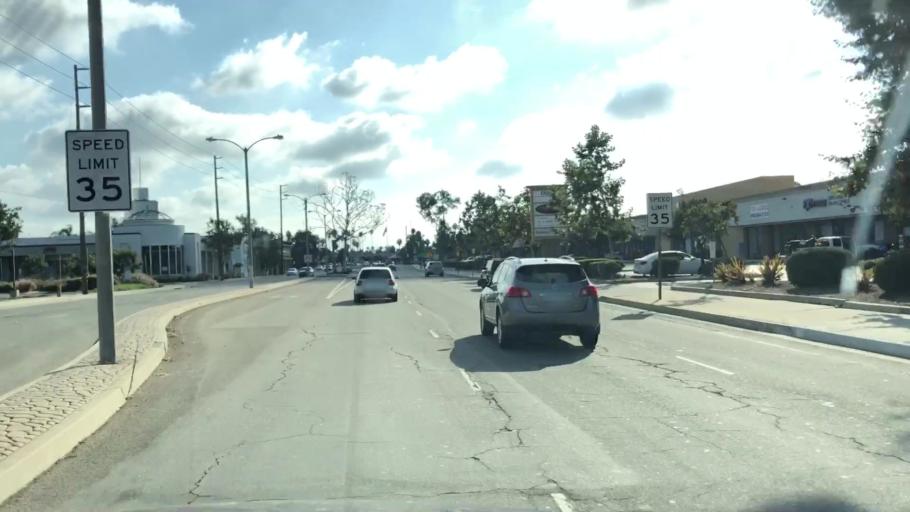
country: US
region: California
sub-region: Ventura County
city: El Rio
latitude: 34.2295
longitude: -119.1752
